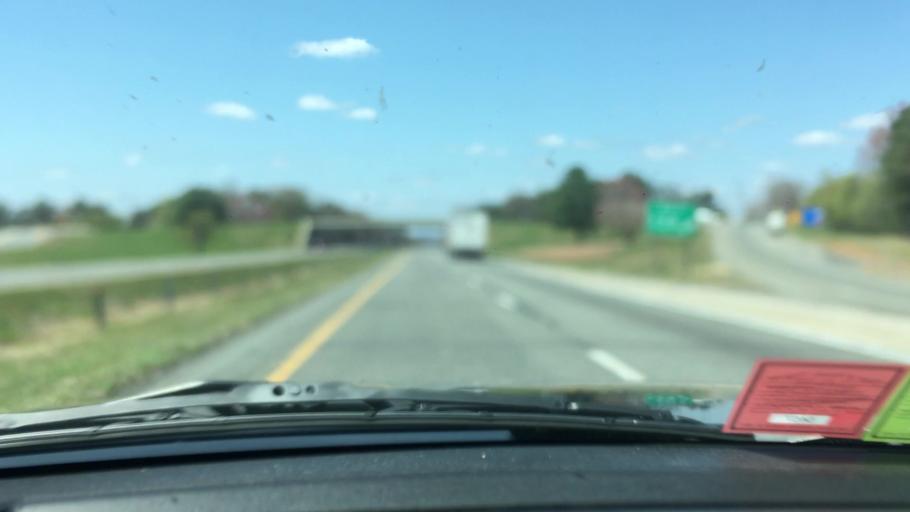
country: US
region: North Carolina
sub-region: Surry County
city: Pilot Mountain
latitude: 36.3744
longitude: -80.4858
